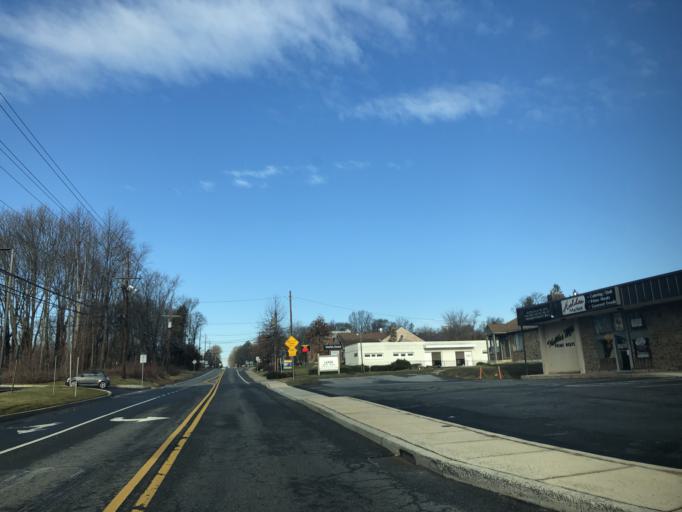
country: US
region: Delaware
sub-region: New Castle County
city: Bellefonte
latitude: 39.8022
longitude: -75.5052
